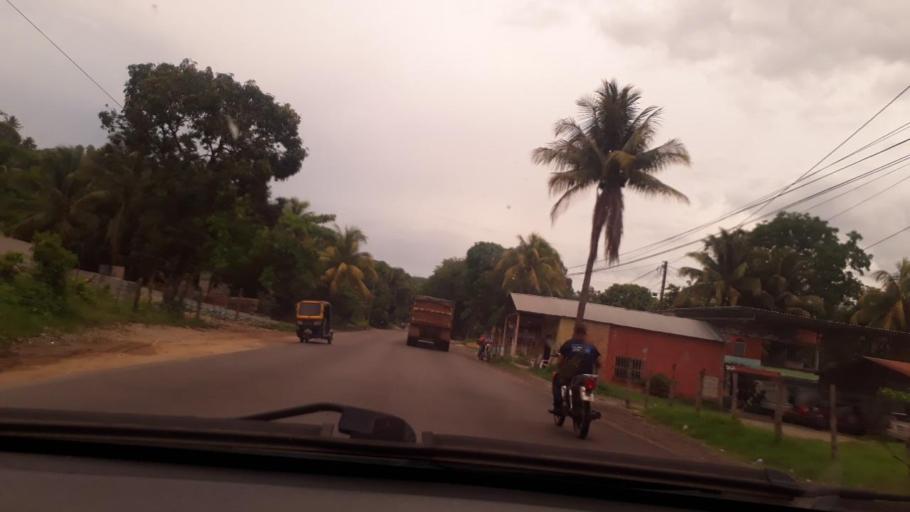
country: GT
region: Izabal
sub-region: Municipio de Los Amates
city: Los Amates
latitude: 15.2705
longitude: -89.0810
